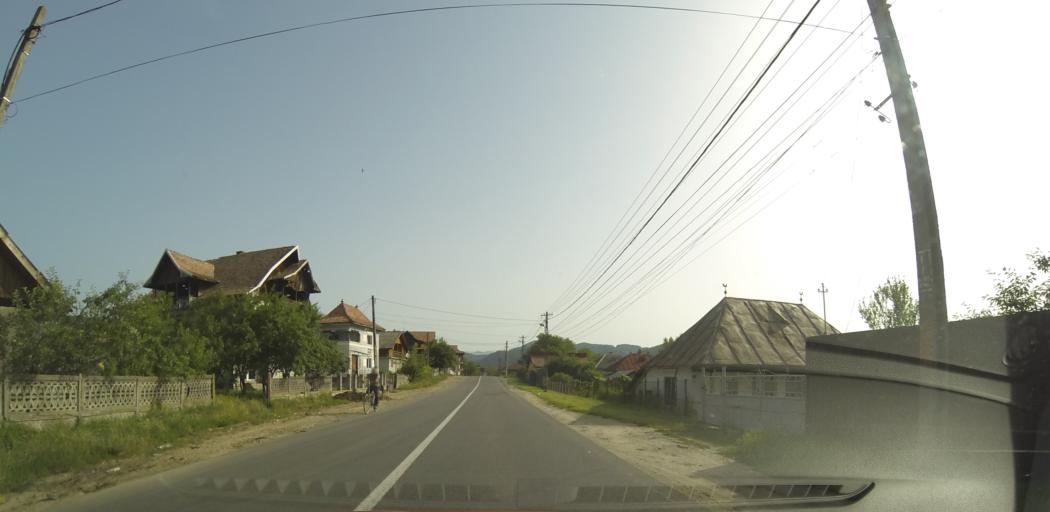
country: RO
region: Valcea
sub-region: Oras Baile Olanesti
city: Olanesti
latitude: 45.1596
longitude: 24.2501
